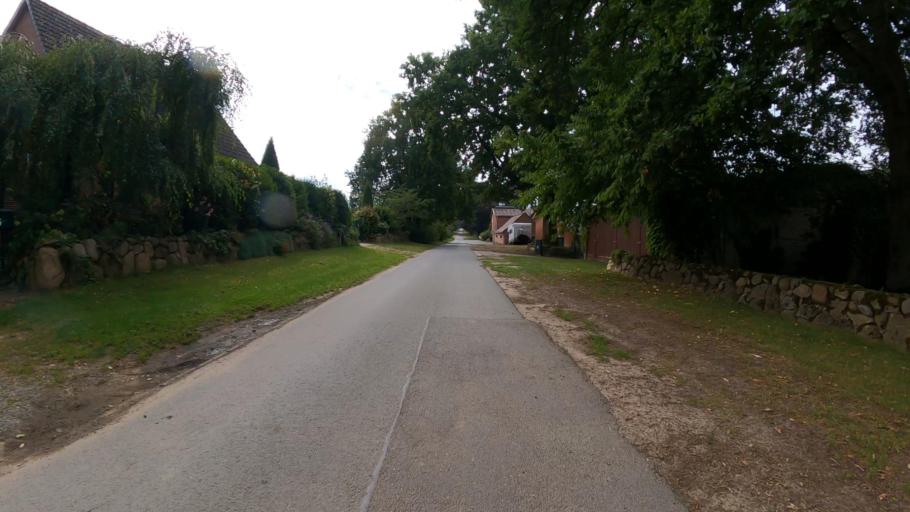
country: DE
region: Lower Saxony
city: Appel
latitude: 53.3779
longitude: 9.7576
